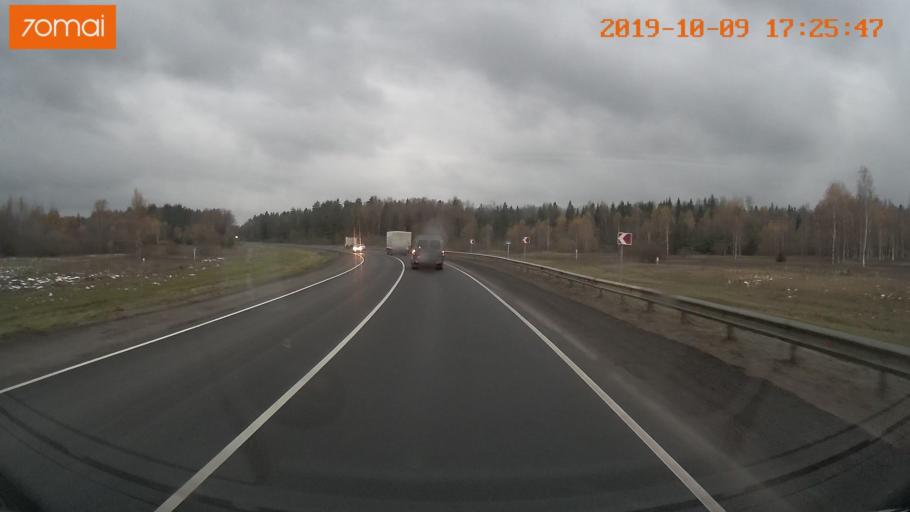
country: RU
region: Ivanovo
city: Furmanov
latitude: 57.1791
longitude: 41.0845
